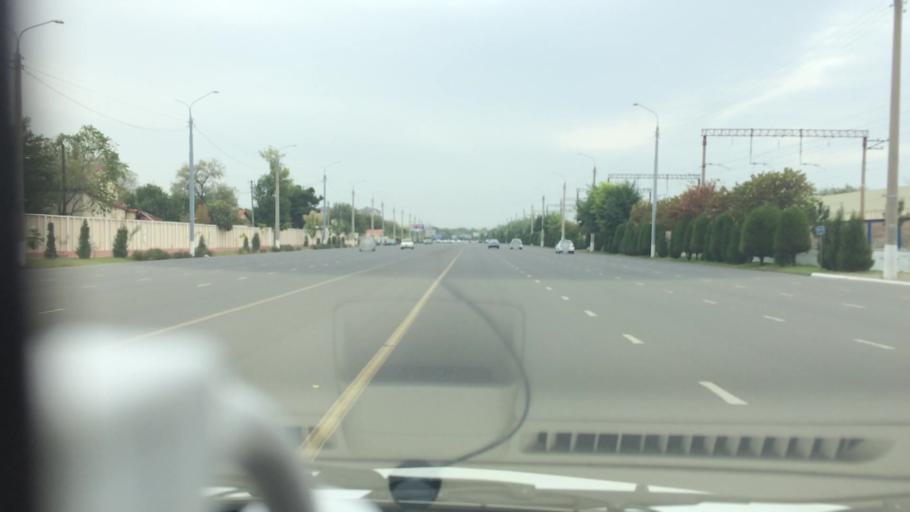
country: UZ
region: Toshkent Shahri
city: Tashkent
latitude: 41.2823
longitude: 69.2765
